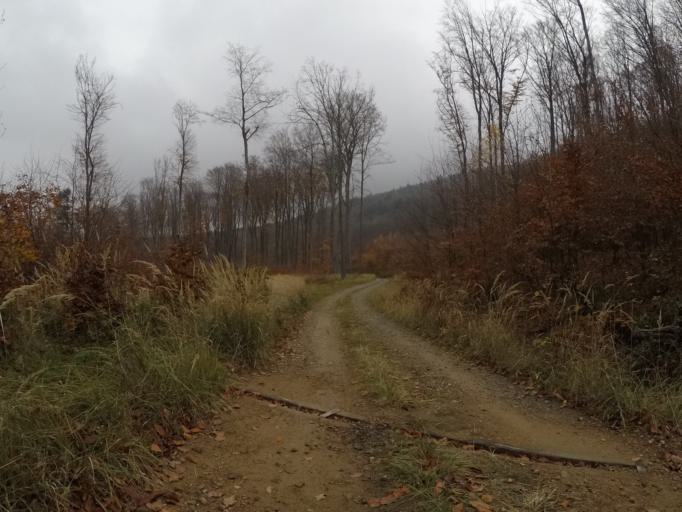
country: SK
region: Presovsky
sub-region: Okres Presov
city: Presov
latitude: 48.8845
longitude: 21.1770
